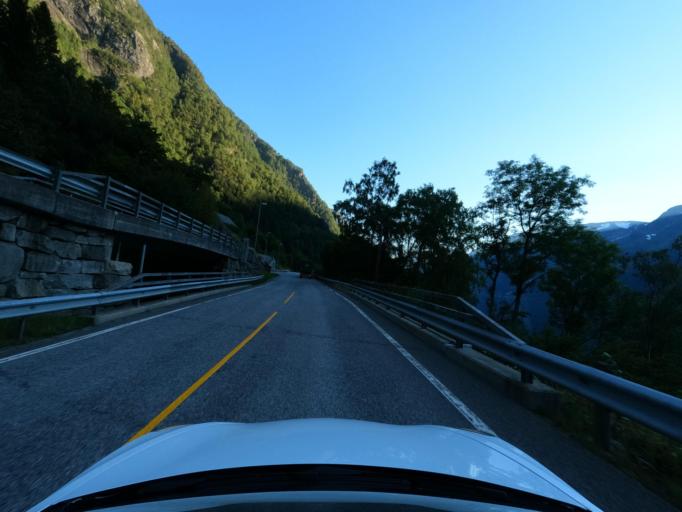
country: NO
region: Hordaland
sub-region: Odda
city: Odda
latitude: 60.1633
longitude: 6.5763
